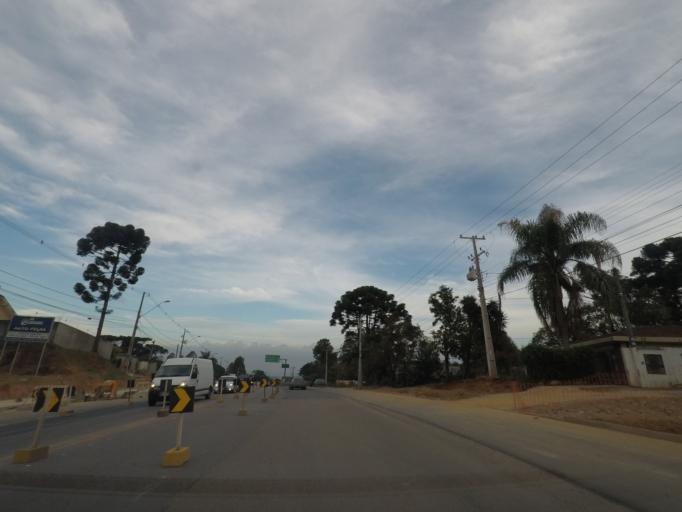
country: BR
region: Parana
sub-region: Colombo
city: Colombo
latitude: -25.3396
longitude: -49.2209
